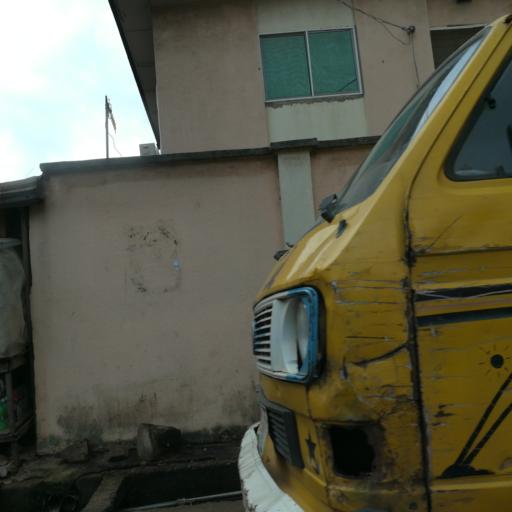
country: NG
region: Lagos
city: Agege
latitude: 6.6066
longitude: 3.3018
